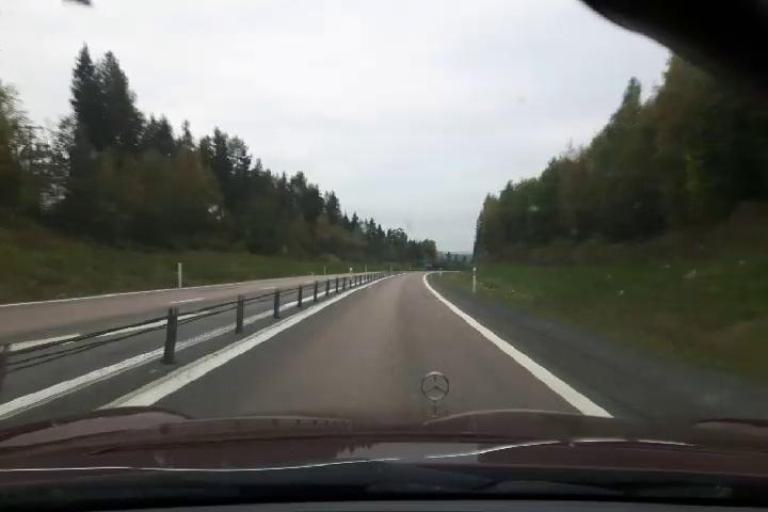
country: SE
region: Vaesternorrland
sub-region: Haernoesands Kommun
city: Haernoesand
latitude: 62.8605
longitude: 18.0274
